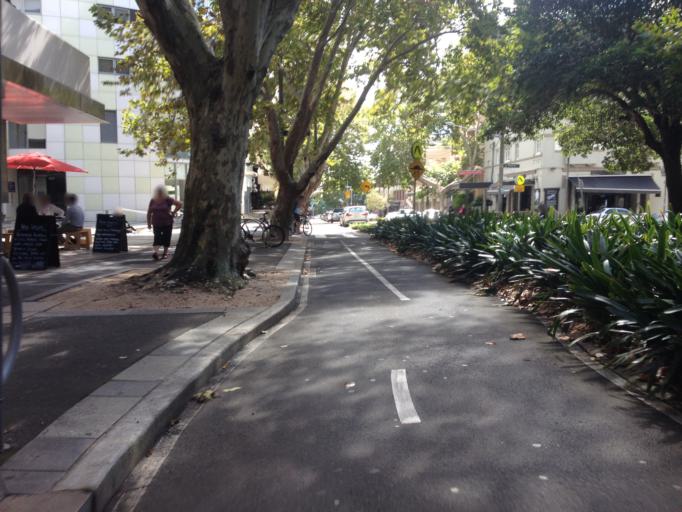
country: AU
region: New South Wales
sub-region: City of Sydney
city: Darlinghurst
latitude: -33.8829
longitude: 151.2163
